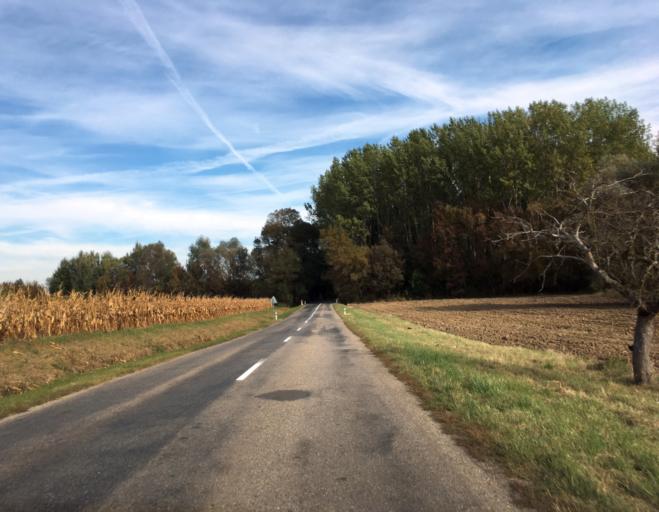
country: SK
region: Nitriansky
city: Svodin
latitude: 48.0036
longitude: 18.4129
